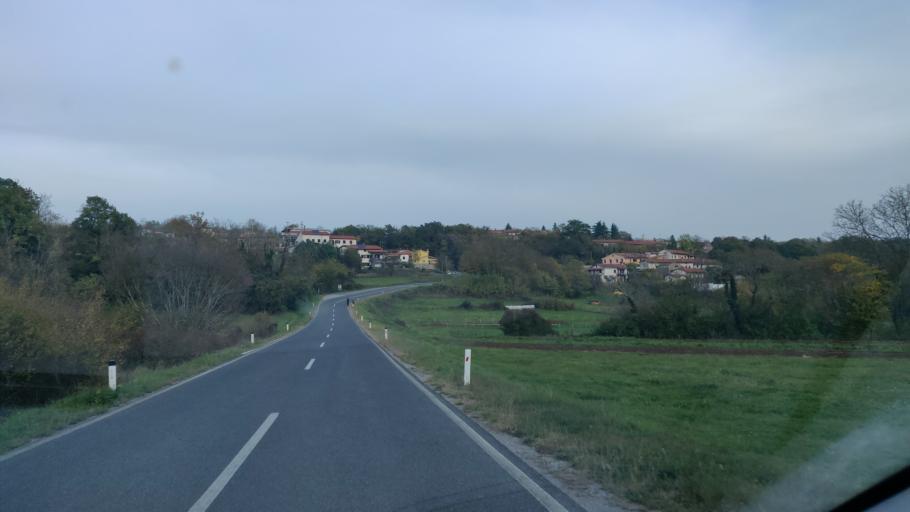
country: SI
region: Komen
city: Komen
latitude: 45.8169
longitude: 13.7657
